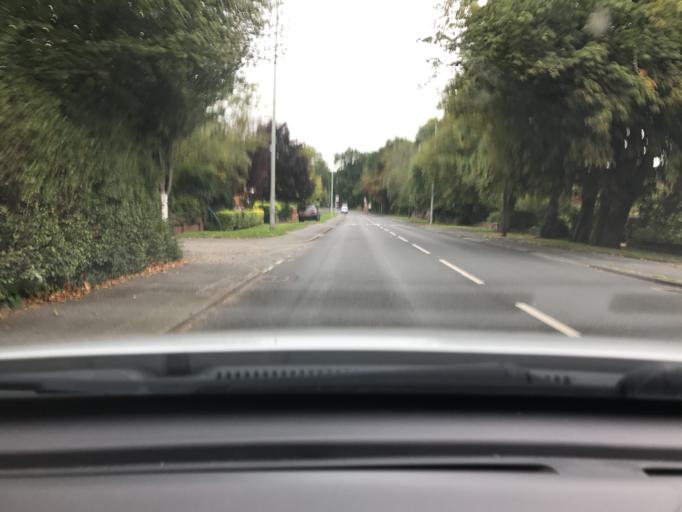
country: GB
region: England
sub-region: Cheshire West and Chester
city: Northwich
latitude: 53.2290
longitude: -2.5094
